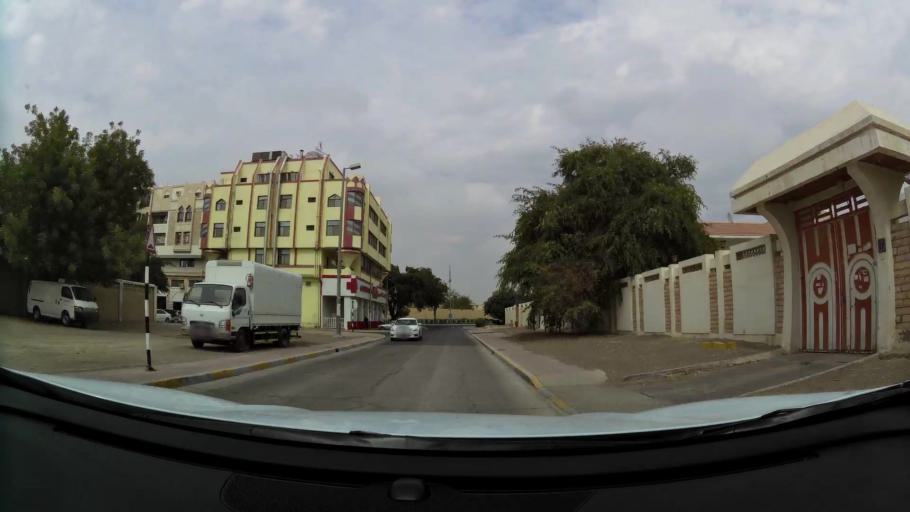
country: AE
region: Abu Dhabi
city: Al Ain
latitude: 24.2203
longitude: 55.7783
